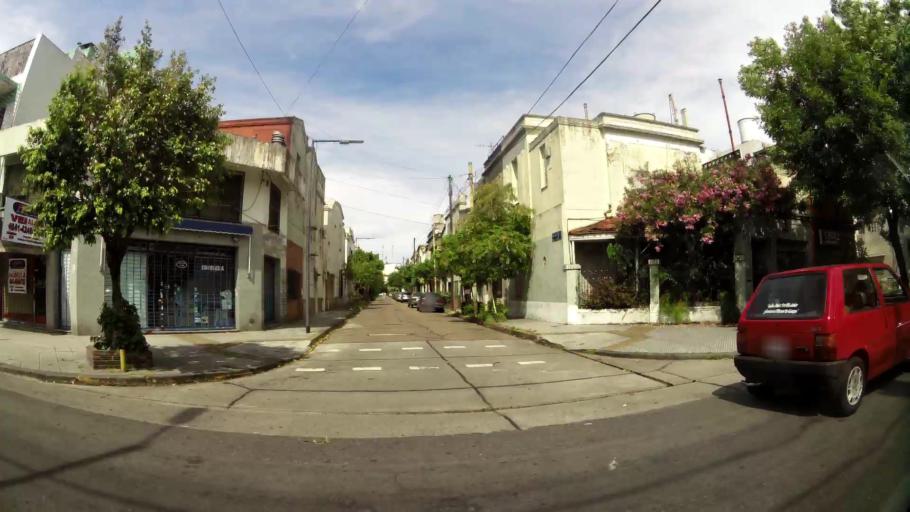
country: AR
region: Buenos Aires
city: San Justo
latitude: -34.6408
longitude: -58.5249
